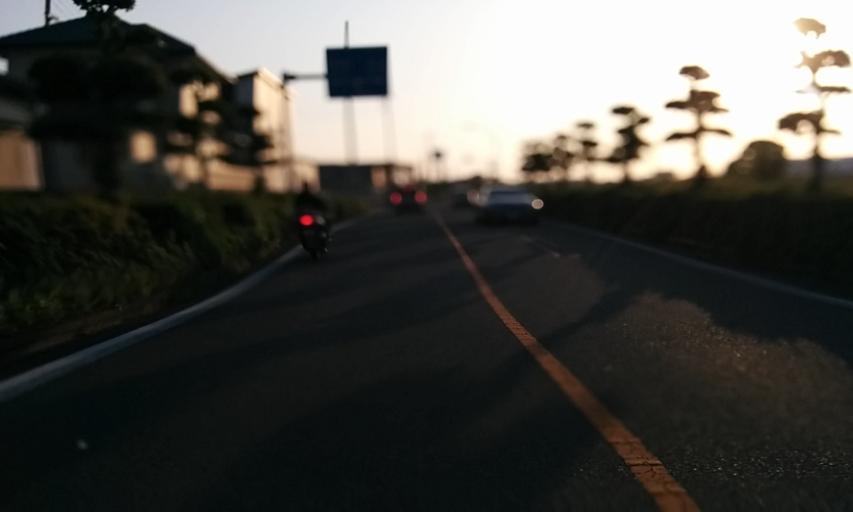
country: JP
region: Ehime
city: Masaki-cho
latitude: 33.7700
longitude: 132.7119
